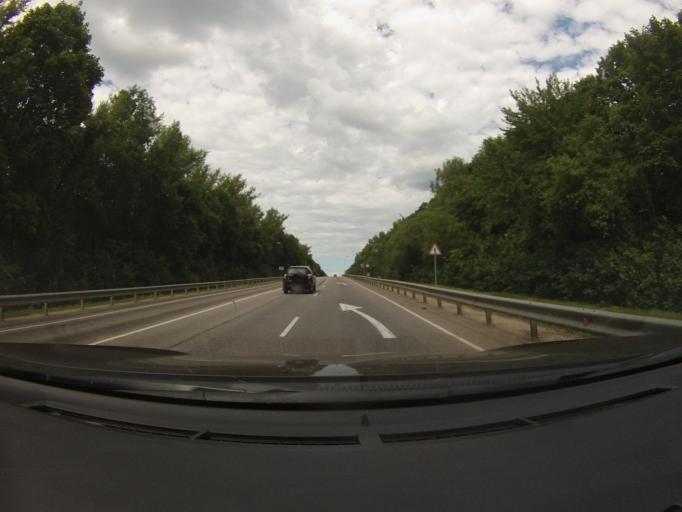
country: RU
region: Orjol
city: Mtsensk
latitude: 53.1906
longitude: 36.4238
